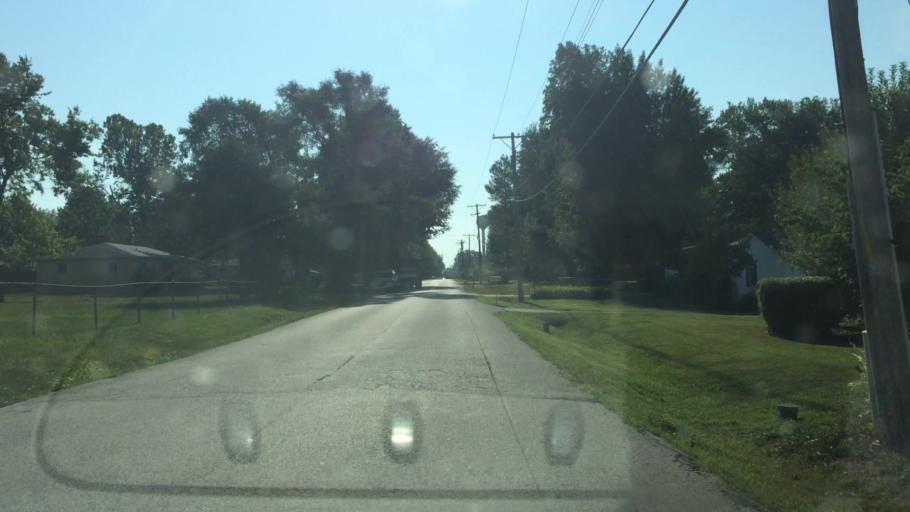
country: US
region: Missouri
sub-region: Greene County
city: Strafford
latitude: 37.2708
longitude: -93.1319
